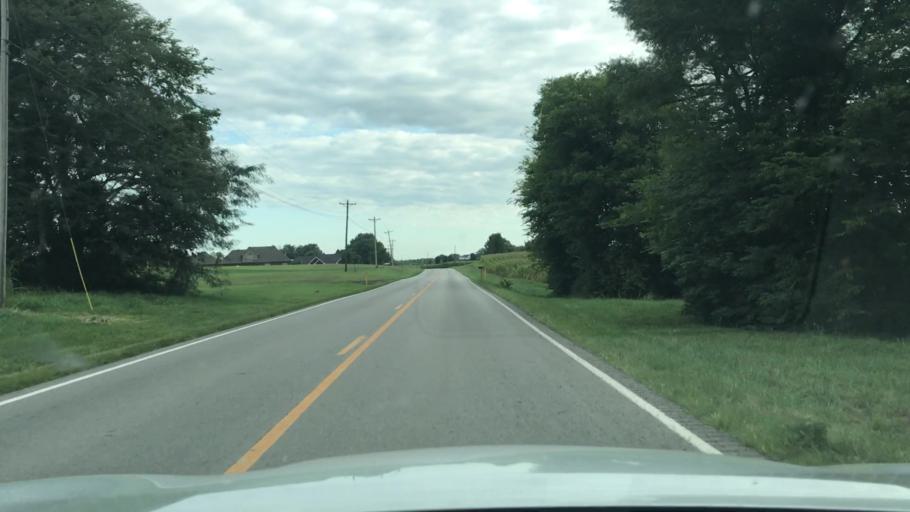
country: US
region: Kentucky
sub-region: Todd County
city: Elkton
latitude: 36.7765
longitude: -87.1649
